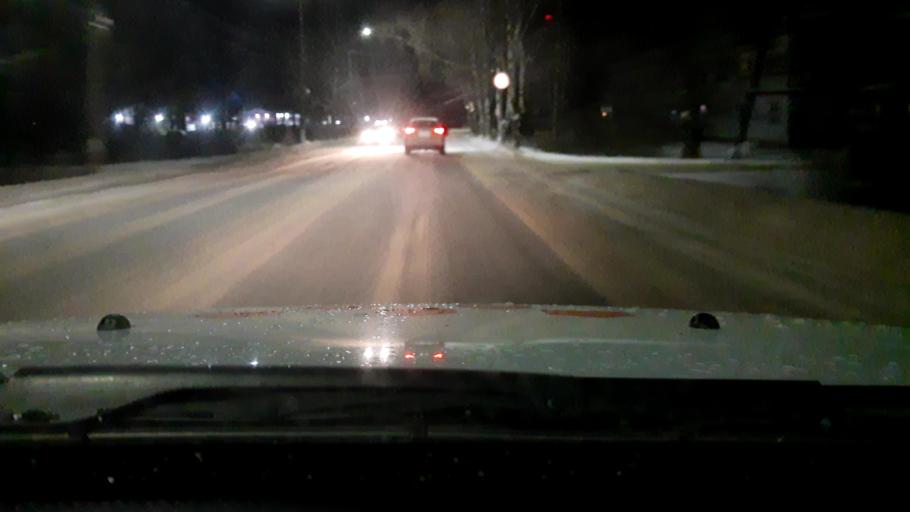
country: RU
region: Nizjnij Novgorod
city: Gorodets
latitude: 56.6555
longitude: 43.4885
